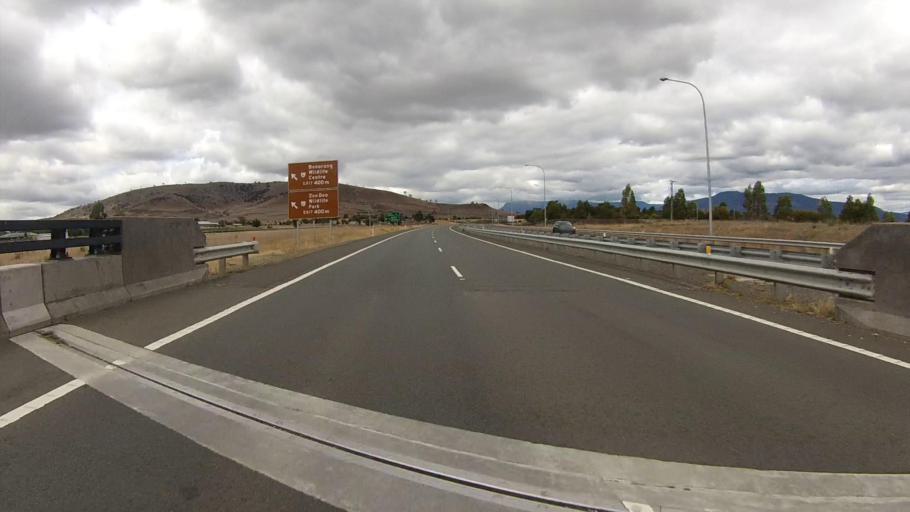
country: AU
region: Tasmania
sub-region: Brighton
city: Bridgewater
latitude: -42.6888
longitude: 147.2785
